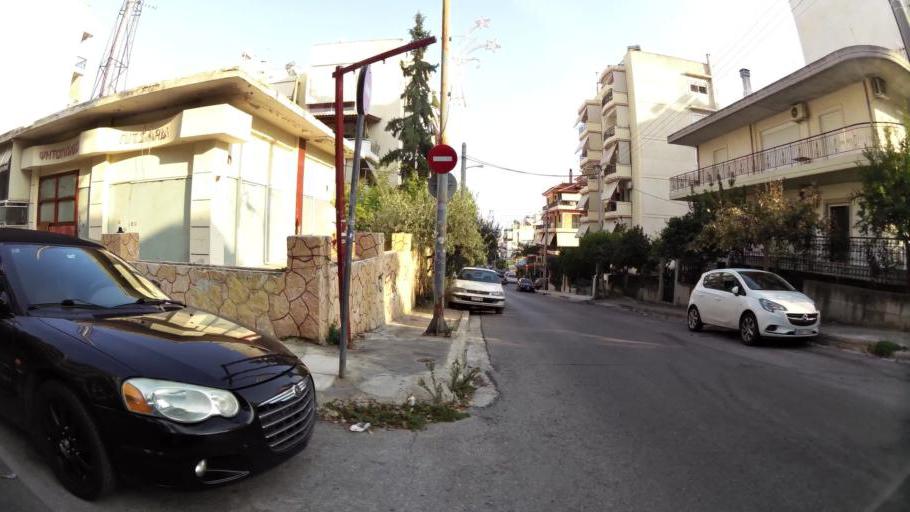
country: GR
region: Attica
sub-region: Nomarchia Athinas
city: Petroupolis
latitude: 38.0419
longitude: 23.6758
